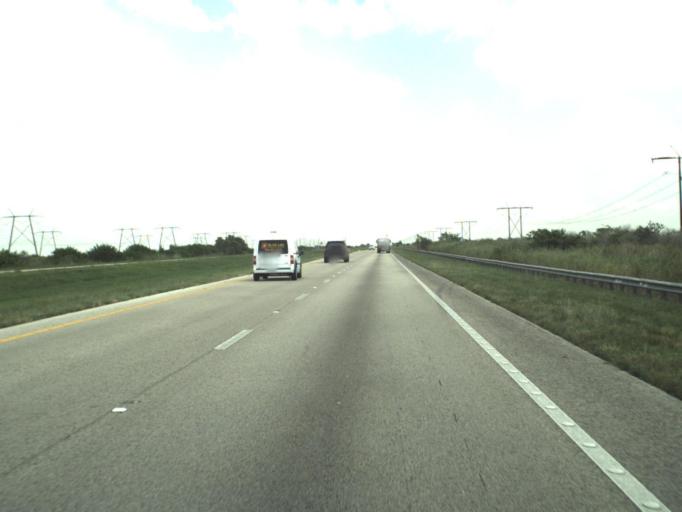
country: US
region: Florida
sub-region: Broward County
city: Weston
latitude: 26.1837
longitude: -80.4503
